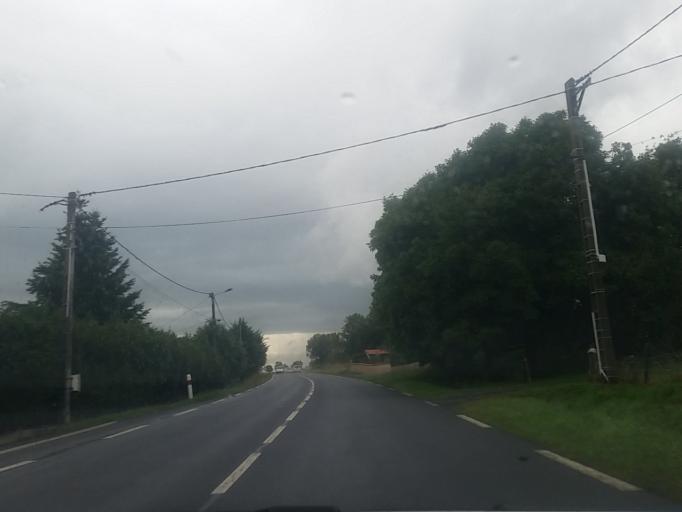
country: FR
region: Auvergne
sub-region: Departement du Cantal
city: Saint-Flour
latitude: 45.0565
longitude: 3.0088
